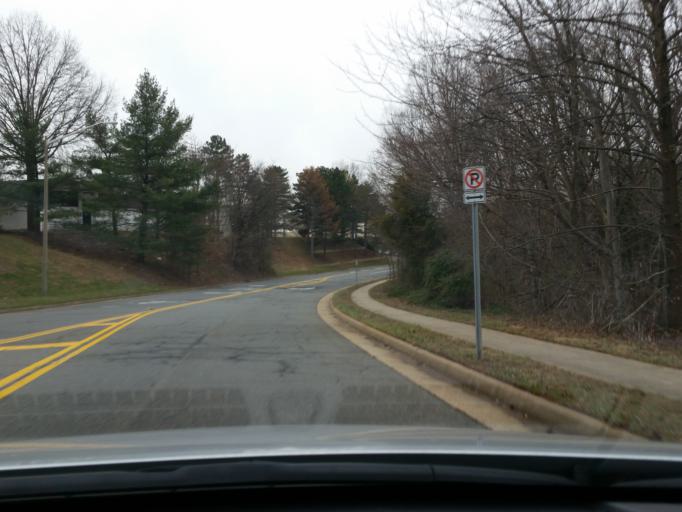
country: US
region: Virginia
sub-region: Fairfax County
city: Reston
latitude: 38.9685
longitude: -77.3556
